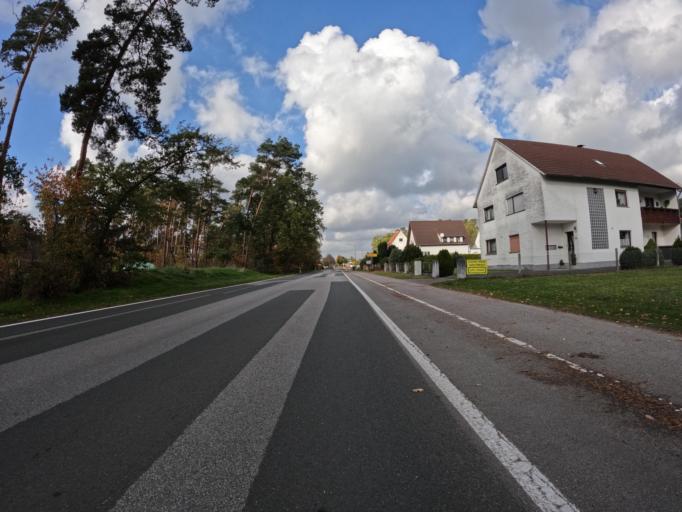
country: DE
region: North Rhine-Westphalia
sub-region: Regierungsbezirk Detmold
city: Hovelhof
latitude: 51.8703
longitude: 8.6477
